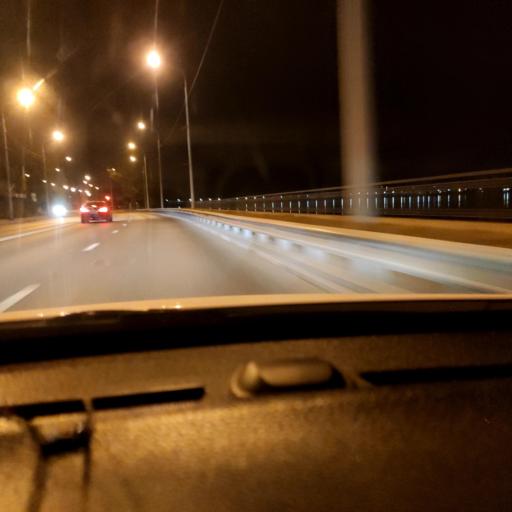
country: RU
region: Voronezj
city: Voronezh
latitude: 51.6770
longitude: 39.2263
